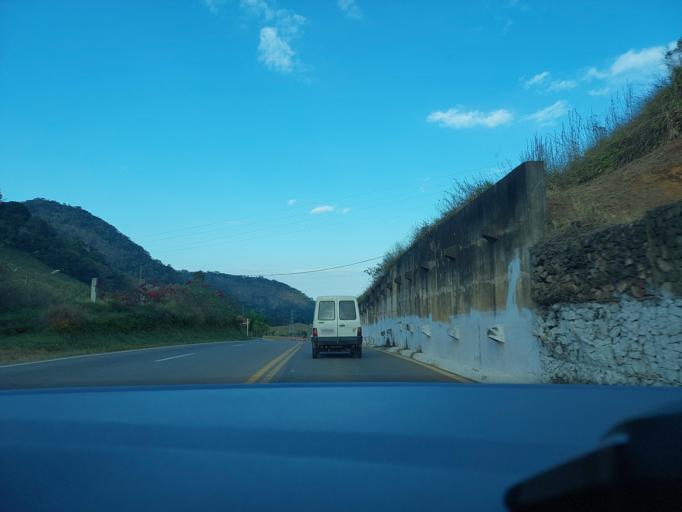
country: BR
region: Minas Gerais
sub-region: Muriae
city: Muriae
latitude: -21.0754
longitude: -42.4985
